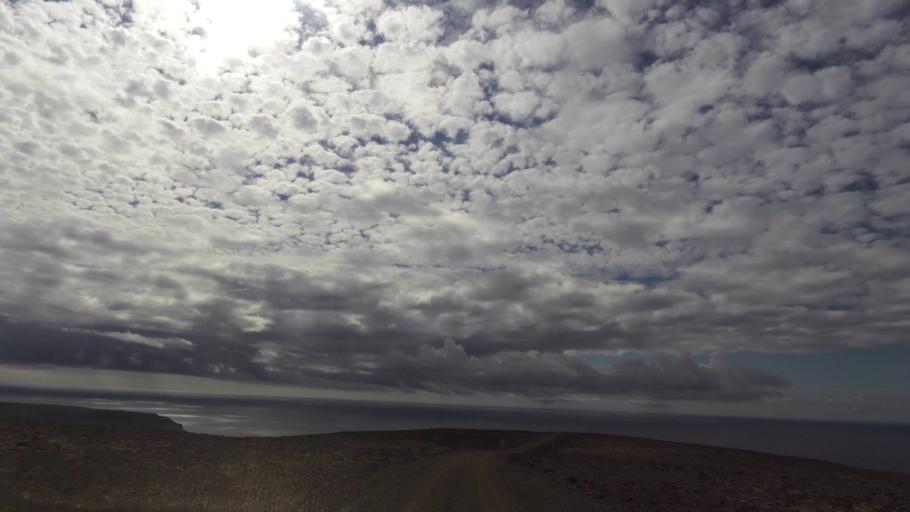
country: IS
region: West
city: Olafsvik
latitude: 65.6207
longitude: -24.3059
